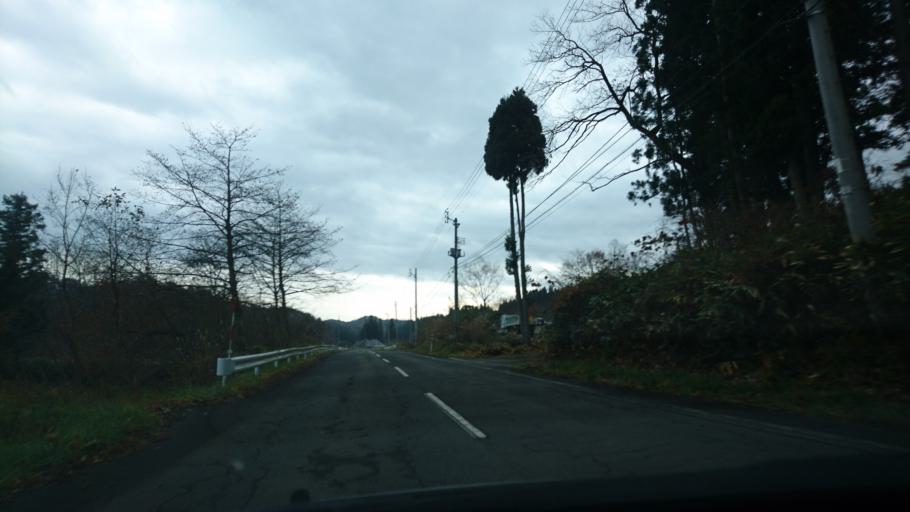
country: JP
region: Iwate
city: Ichinoseki
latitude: 38.9368
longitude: 140.9203
